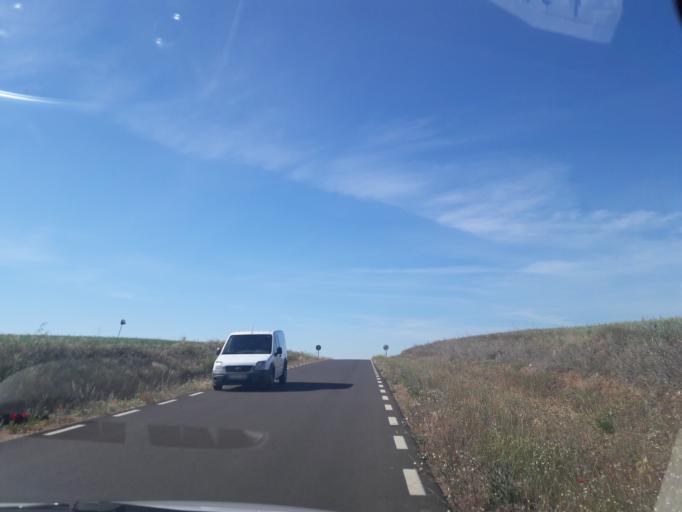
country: ES
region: Castille and Leon
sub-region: Provincia de Salamanca
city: Parada de Rubiales
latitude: 41.1363
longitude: -5.4304
